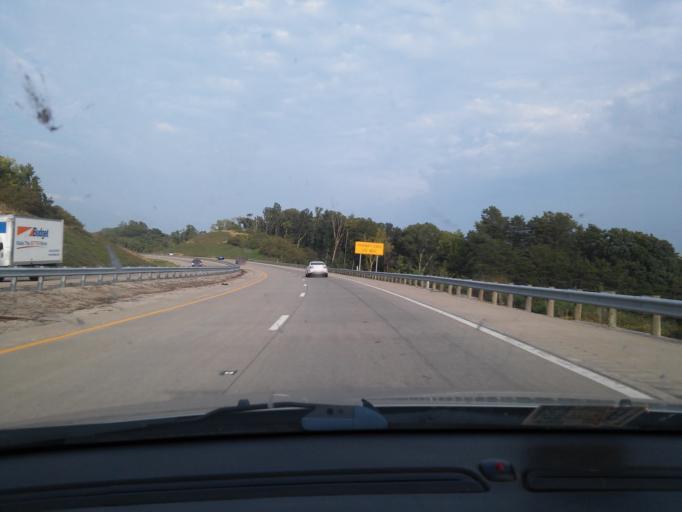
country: US
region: West Virginia
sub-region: Mason County
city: Point Pleasant
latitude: 38.7642
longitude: -82.0209
